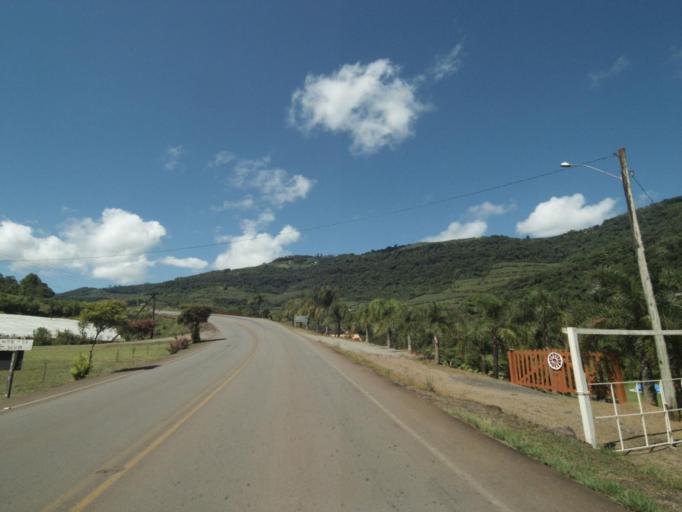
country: BR
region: Rio Grande do Sul
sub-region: Bento Goncalves
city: Bento Goncalves
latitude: -29.0967
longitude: -51.6270
